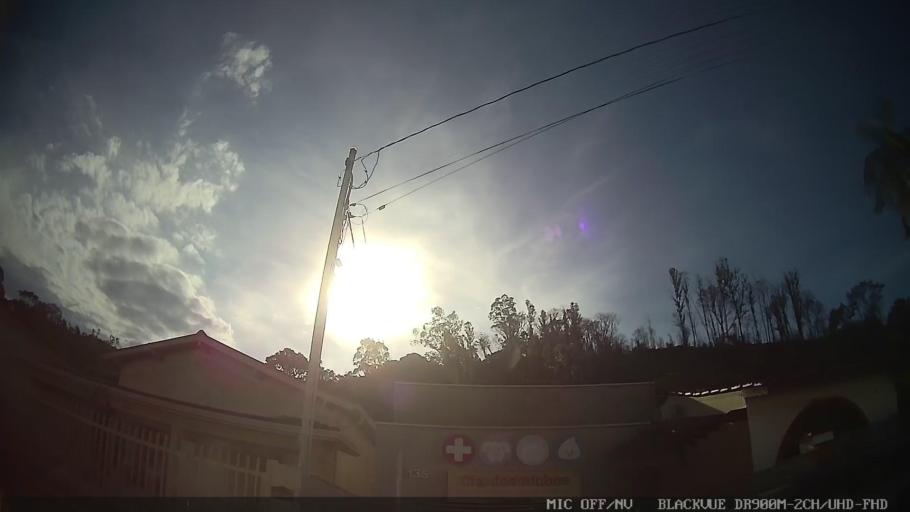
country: BR
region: Sao Paulo
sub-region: Serra Negra
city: Serra Negra
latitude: -22.6790
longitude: -46.6807
